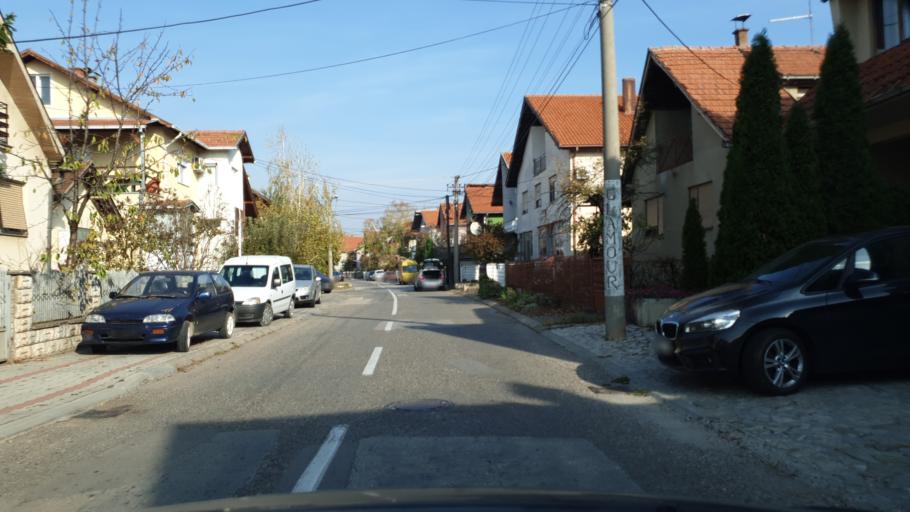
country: RS
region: Central Serbia
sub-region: Pomoravski Okrug
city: Paracin
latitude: 43.8557
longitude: 21.4245
